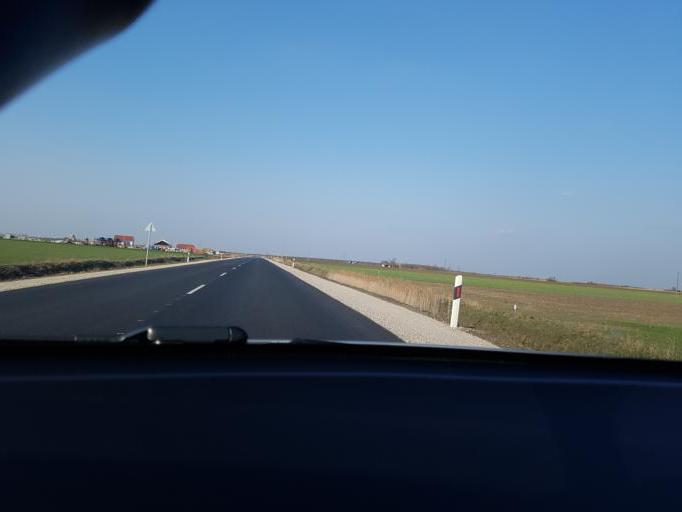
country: RO
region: Arad
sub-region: Comuna Nadlac
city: Nadlac
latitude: 46.2005
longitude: 20.7159
